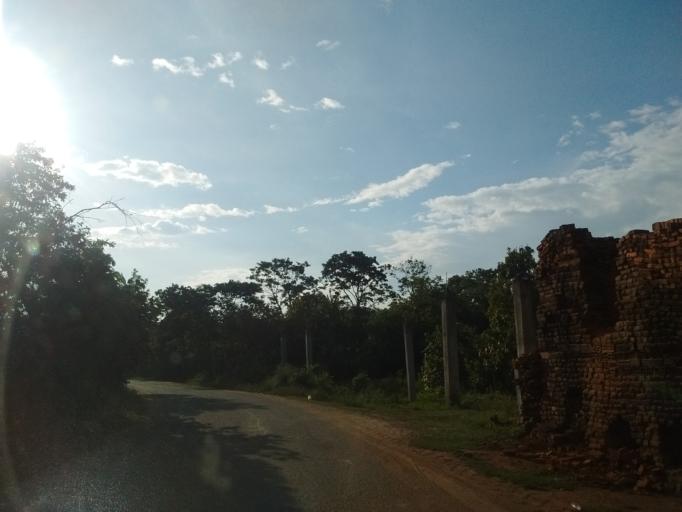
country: CO
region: Cauca
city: Puerto Tejada
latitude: 3.2017
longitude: -76.4439
